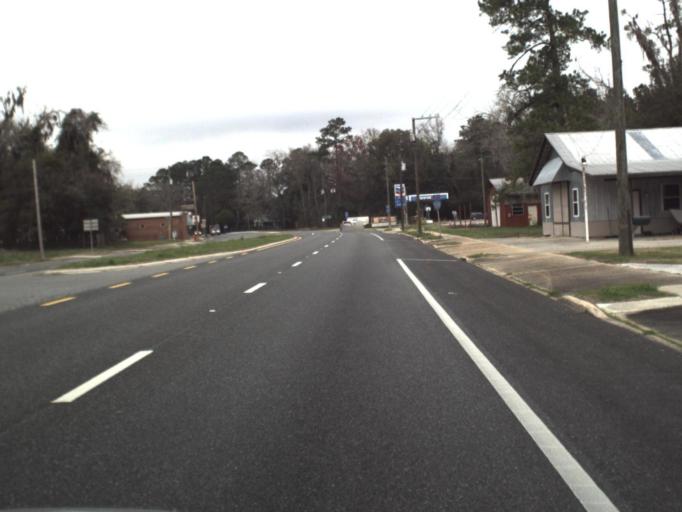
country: US
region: Florida
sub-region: Jefferson County
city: Monticello
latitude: 30.3762
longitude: -83.8118
